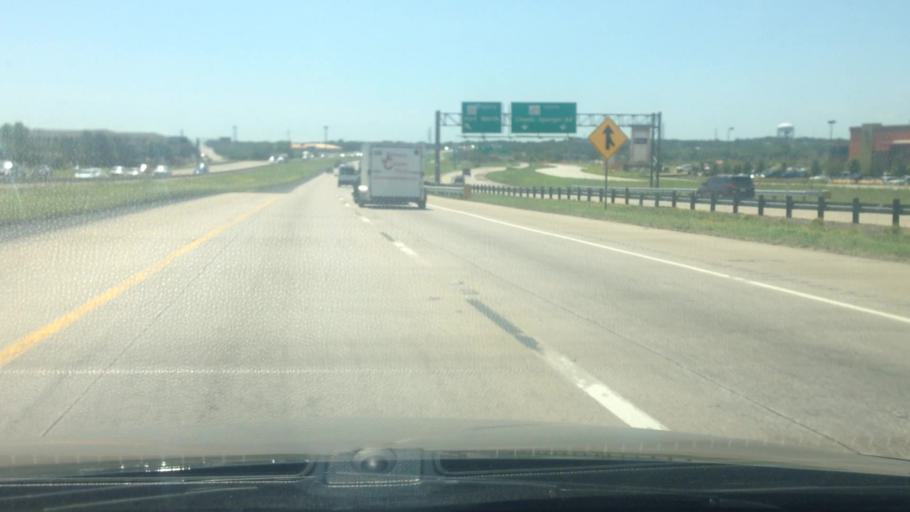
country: US
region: Texas
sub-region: Tarrant County
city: Euless
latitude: 32.8755
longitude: -97.0996
